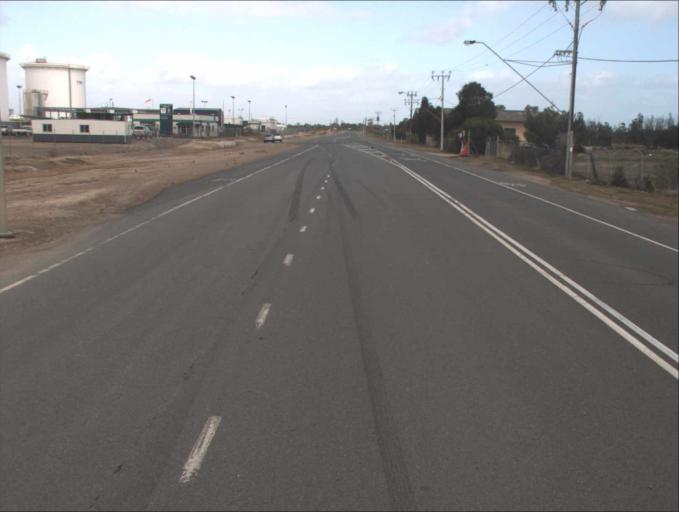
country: AU
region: South Australia
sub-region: Port Adelaide Enfield
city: Birkenhead
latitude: -34.7733
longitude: 138.5016
